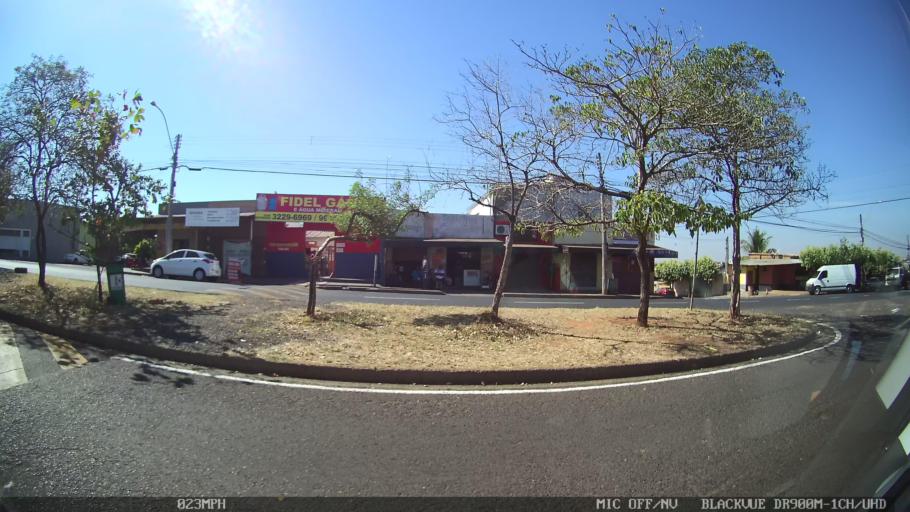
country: BR
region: Sao Paulo
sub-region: Sao Jose Do Rio Preto
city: Sao Jose do Rio Preto
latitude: -20.7549
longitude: -49.4054
